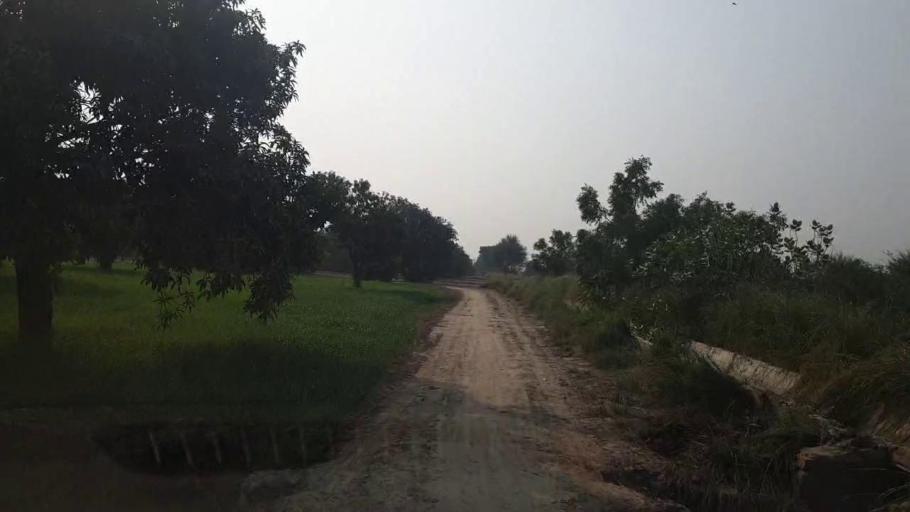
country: PK
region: Sindh
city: Tando Jam
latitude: 25.3284
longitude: 68.5201
